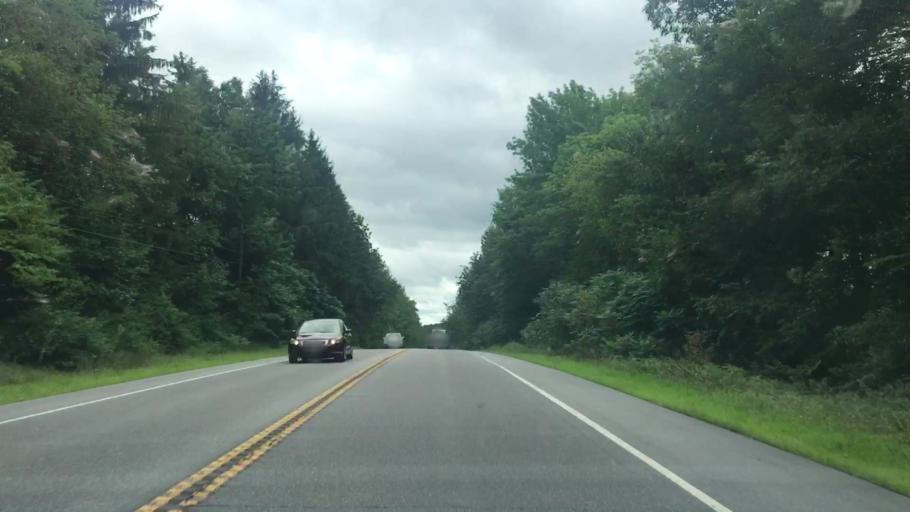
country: US
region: Maine
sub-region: York County
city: Alfred
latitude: 43.5024
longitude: -70.7177
